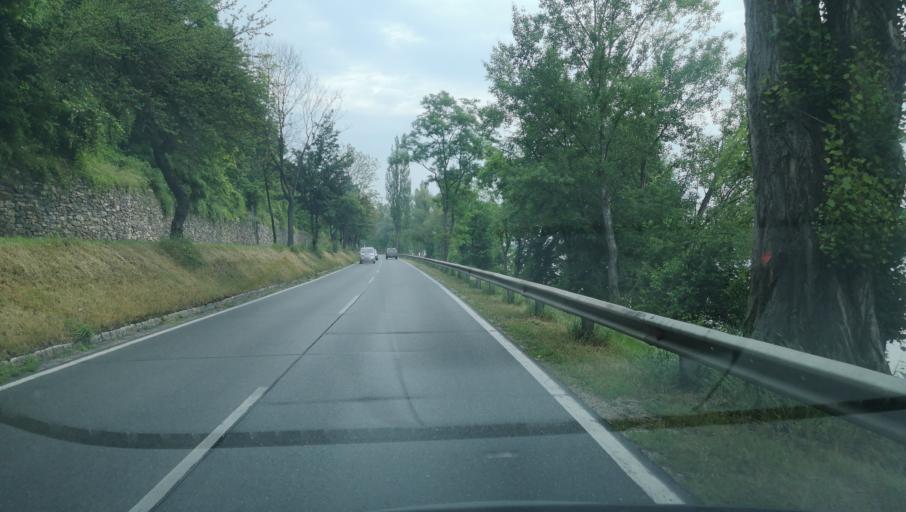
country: AT
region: Lower Austria
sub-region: Politischer Bezirk Krems
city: Weinzierl bei Krems
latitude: 48.3947
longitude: 15.5631
